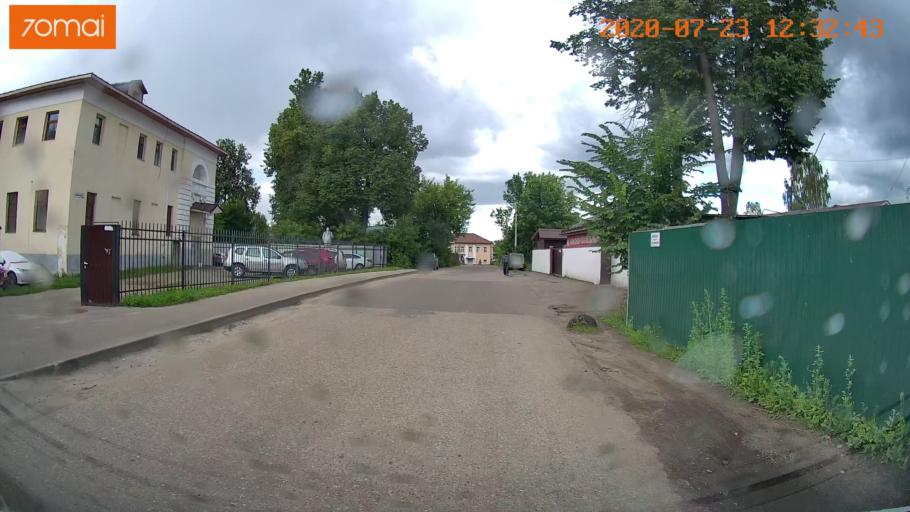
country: RU
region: Ivanovo
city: Bogorodskoye
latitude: 57.0468
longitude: 41.0059
